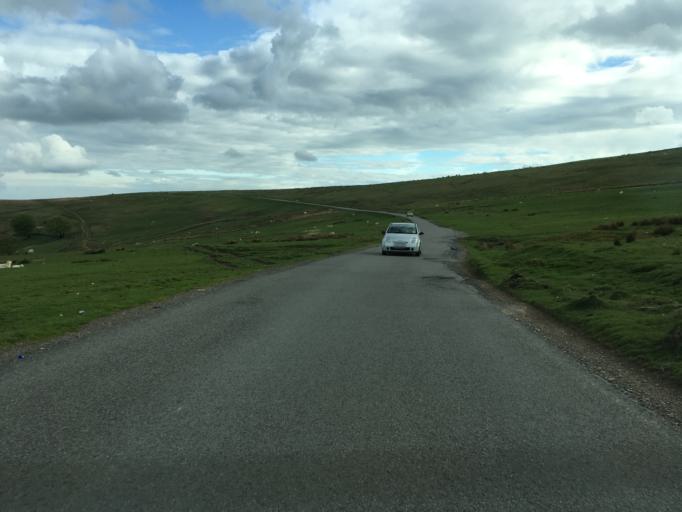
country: GB
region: Wales
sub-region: Caerphilly County Borough
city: Rhymney
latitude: 51.7263
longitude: -3.2972
